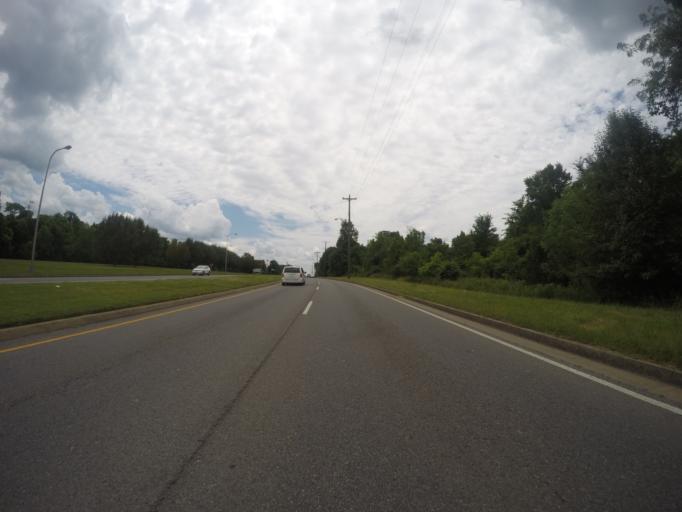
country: US
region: Tennessee
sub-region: Davidson County
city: Lakewood
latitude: 36.2071
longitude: -86.6229
